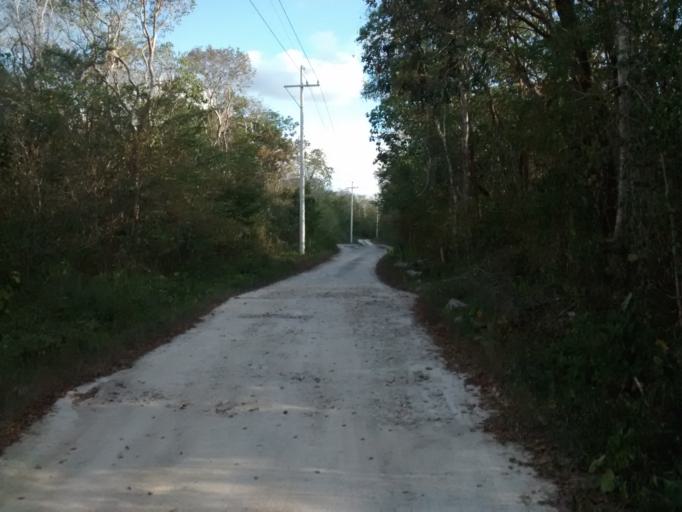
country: MX
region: Yucatan
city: Chichimila
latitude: 20.4516
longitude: -88.2033
